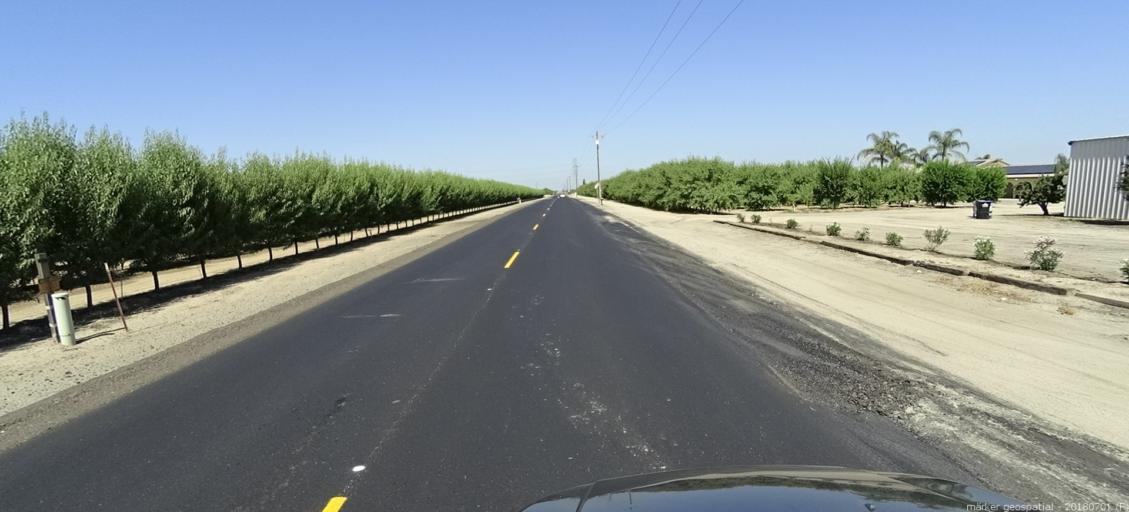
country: US
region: California
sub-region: Madera County
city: Parksdale
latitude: 36.8803
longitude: -119.9425
